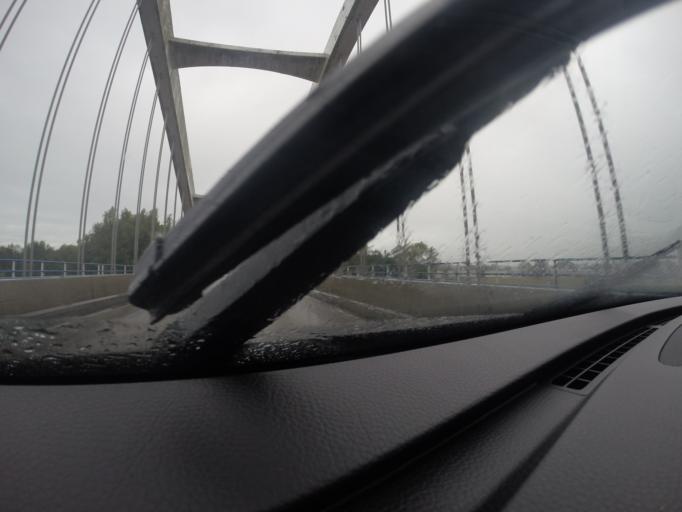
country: NL
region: Gelderland
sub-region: Gemeente Lochem
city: Lochem
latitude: 52.1667
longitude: 6.3950
